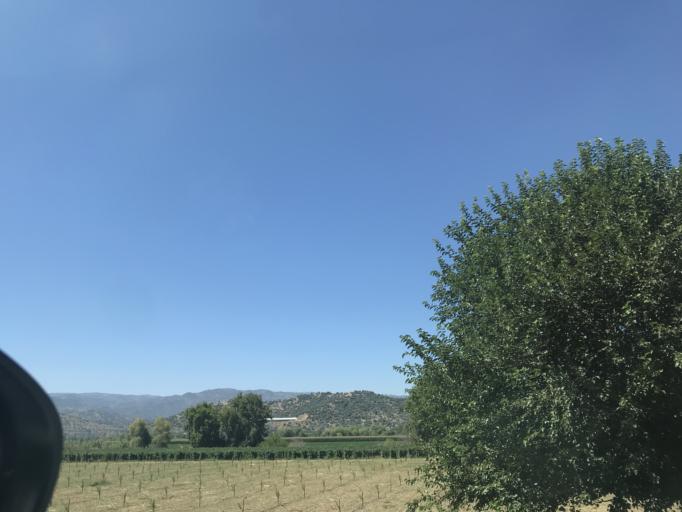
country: TR
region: Aydin
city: Cakirbeyli
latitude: 37.7558
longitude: 27.8495
